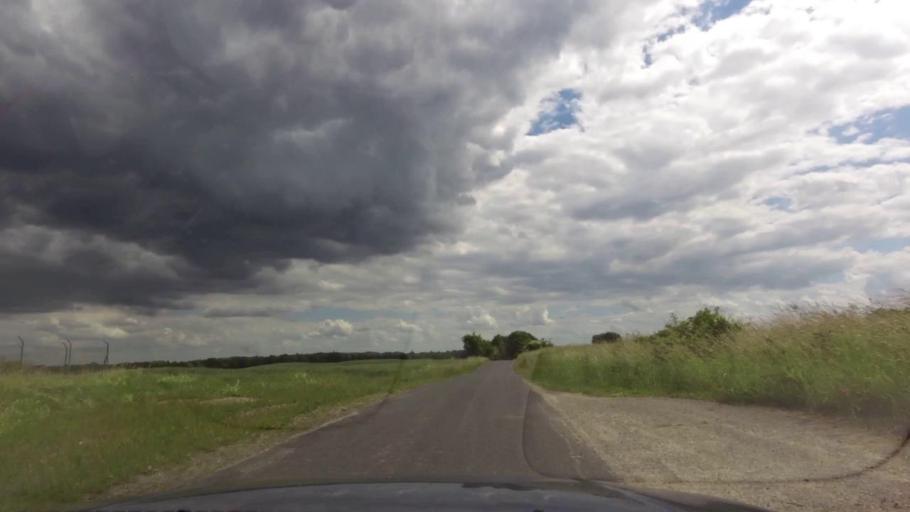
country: PL
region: West Pomeranian Voivodeship
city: Trzcinsko Zdroj
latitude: 52.9081
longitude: 14.6025
